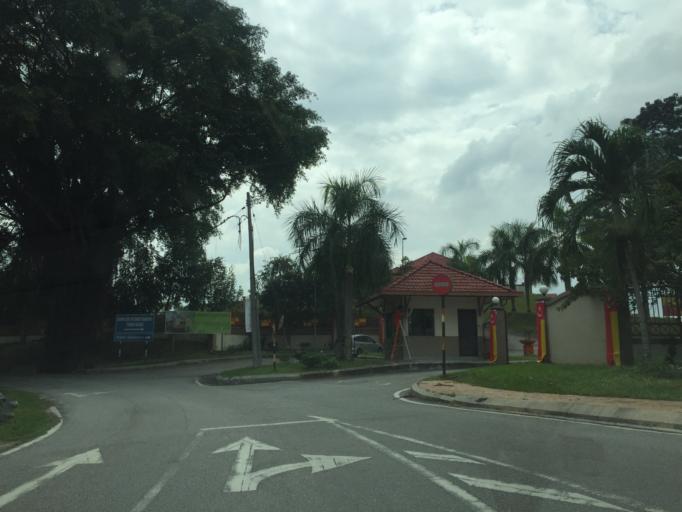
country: MY
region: Selangor
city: Klang
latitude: 3.0409
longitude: 101.4437
